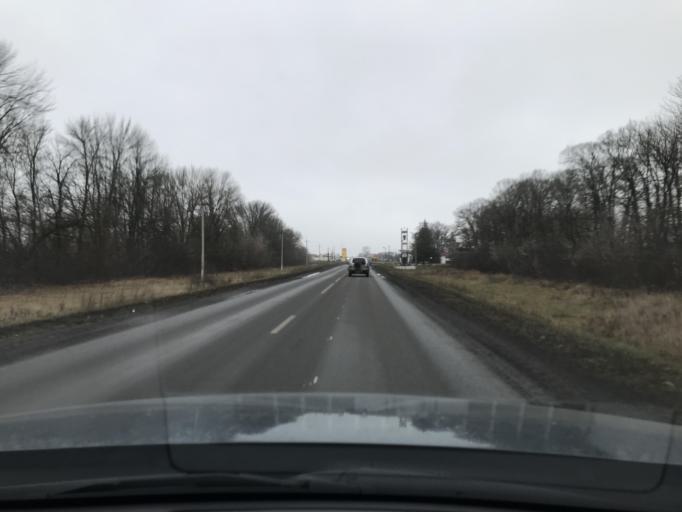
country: RU
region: Penza
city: Zemetchino
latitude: 53.5126
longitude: 42.6419
